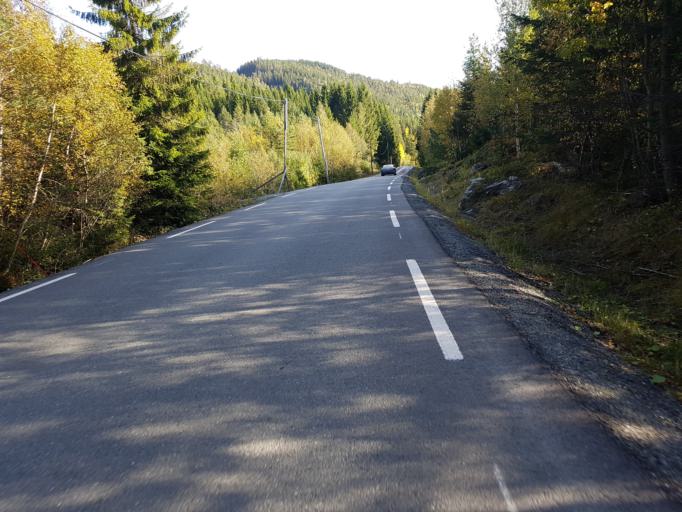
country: NO
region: Sor-Trondelag
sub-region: Malvik
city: Malvik
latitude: 63.3773
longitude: 10.6033
